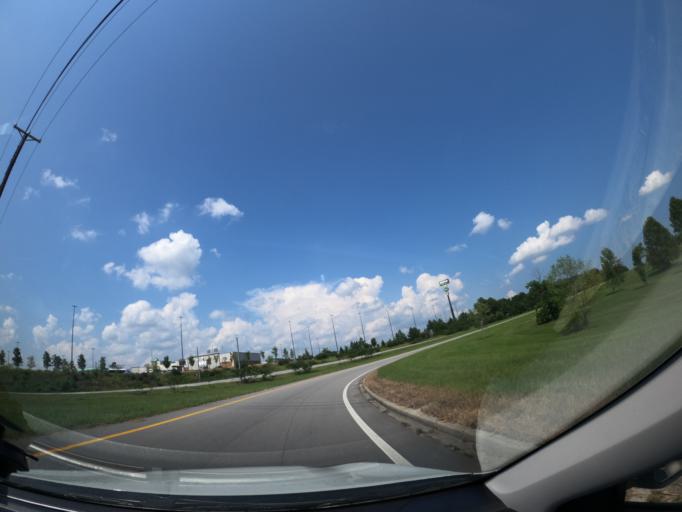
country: US
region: South Carolina
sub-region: Richland County
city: Columbia
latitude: 33.9515
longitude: -80.9906
